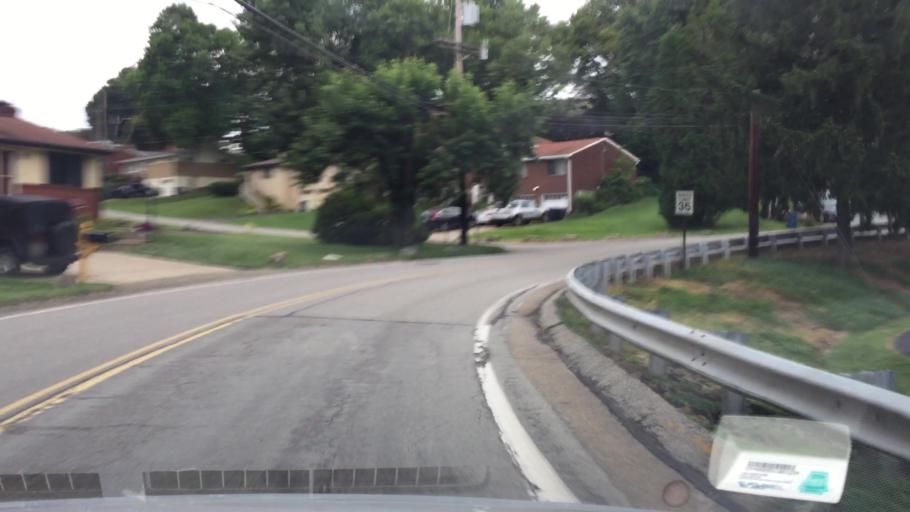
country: US
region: Pennsylvania
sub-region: Allegheny County
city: Glenshaw
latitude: 40.5197
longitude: -79.9847
